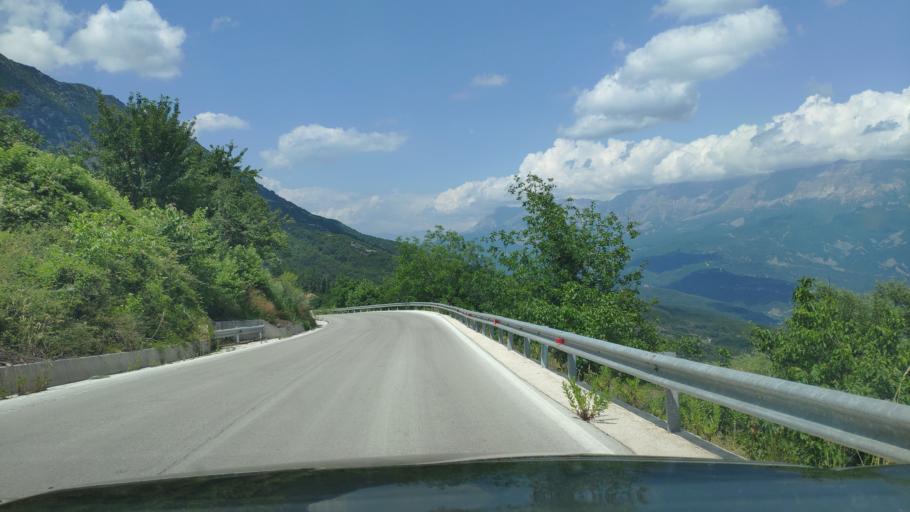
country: GR
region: Epirus
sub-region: Nomos Artas
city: Agios Dimitrios
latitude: 39.3379
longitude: 21.0060
